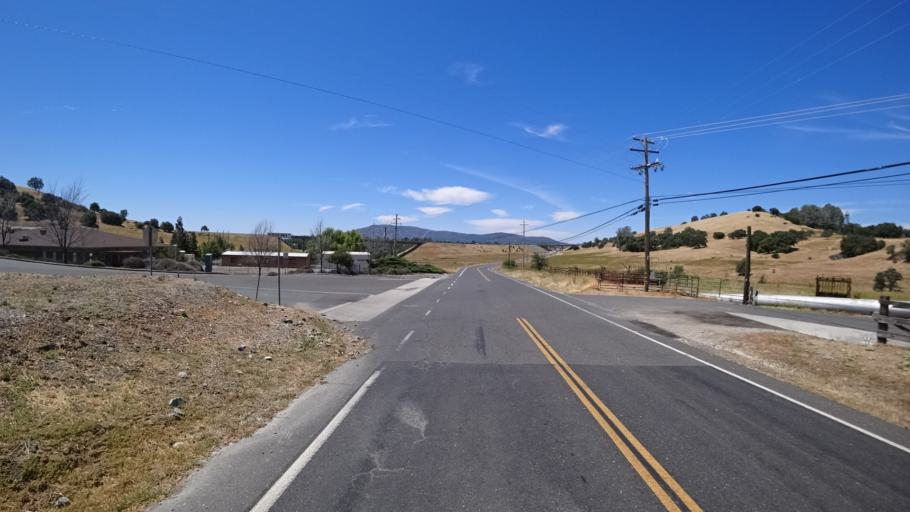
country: US
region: California
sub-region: Calaveras County
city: Angels Camp
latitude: 38.0865
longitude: -120.5399
